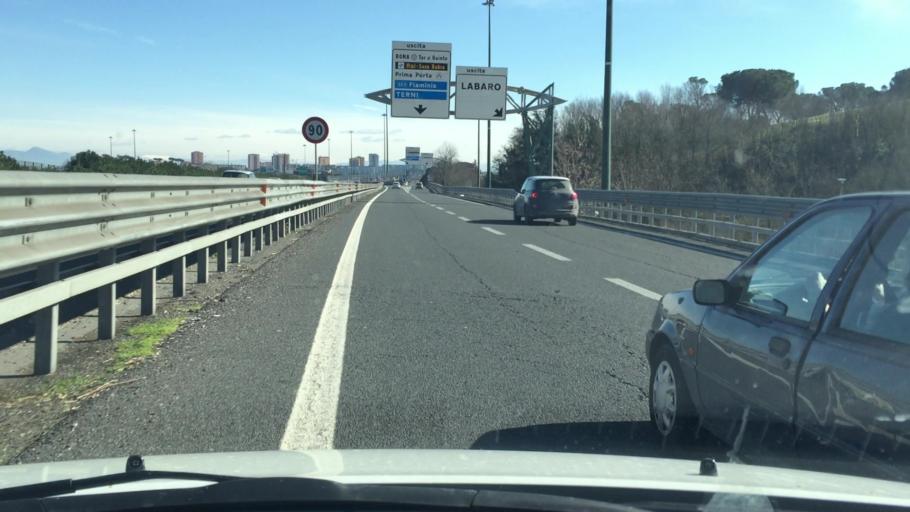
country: IT
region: Latium
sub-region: Citta metropolitana di Roma Capitale
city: Monte Caminetto
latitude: 41.9860
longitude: 12.4849
